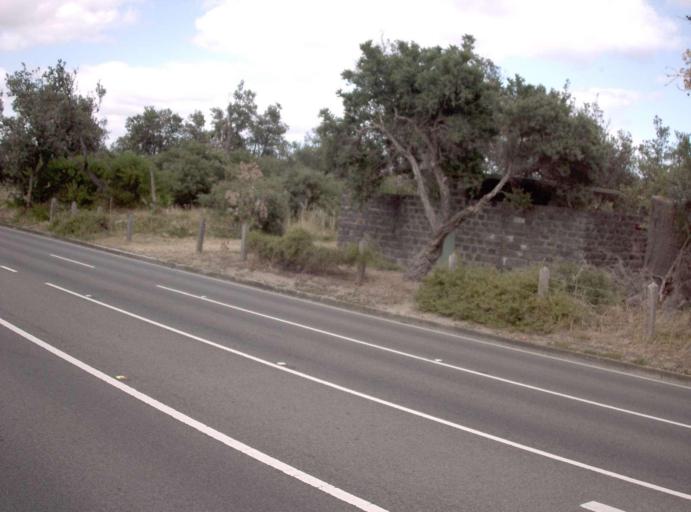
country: AU
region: Victoria
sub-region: Frankston
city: Frankston East
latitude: -38.1211
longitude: 145.1249
